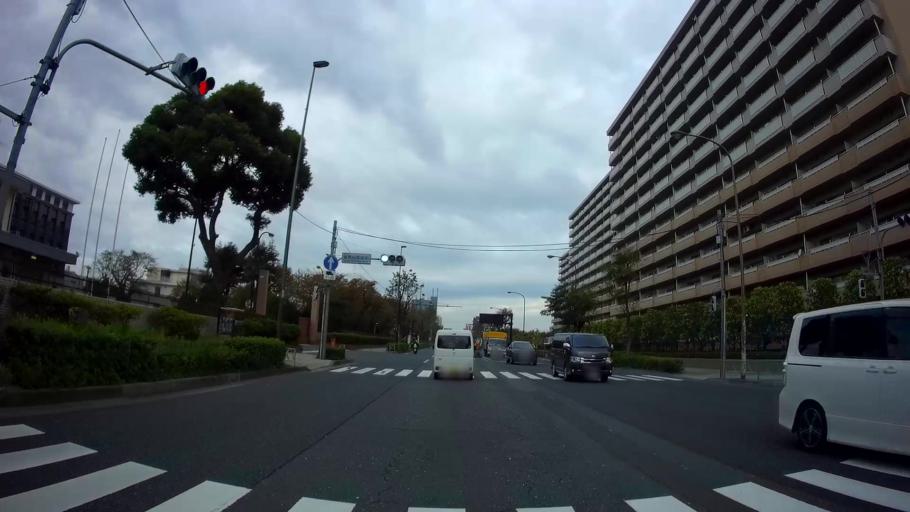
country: JP
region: Saitama
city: Wako
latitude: 35.7650
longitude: 139.6609
